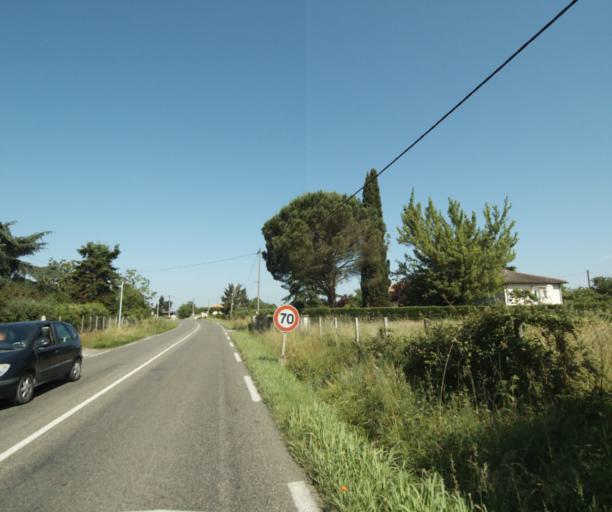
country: FR
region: Midi-Pyrenees
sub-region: Departement du Tarn-et-Garonne
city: Montbeton
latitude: 44.0172
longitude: 1.3065
